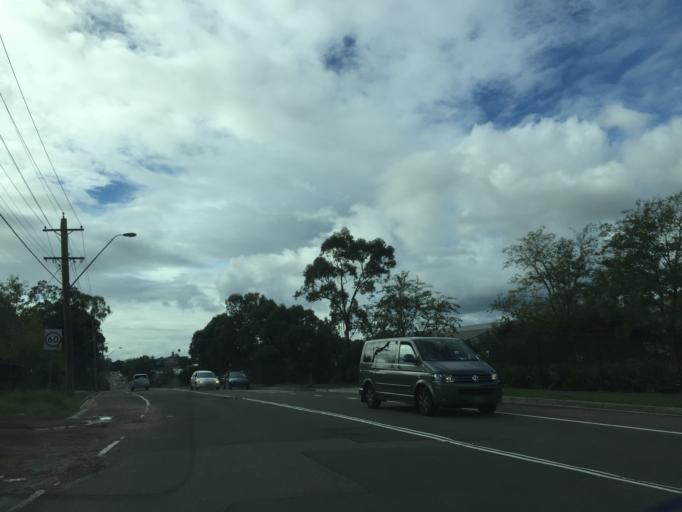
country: AU
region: New South Wales
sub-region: Blacktown
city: Doonside
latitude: -33.7955
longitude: 150.8893
